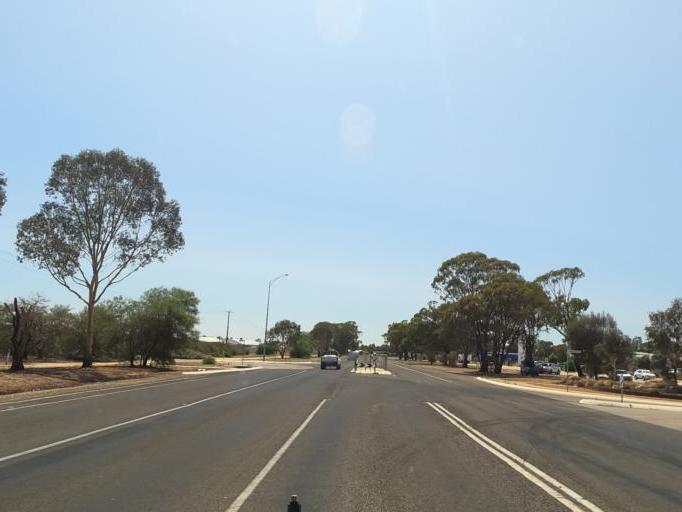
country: AU
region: Victoria
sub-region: Moira
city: Yarrawonga
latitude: -36.0116
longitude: 146.0246
